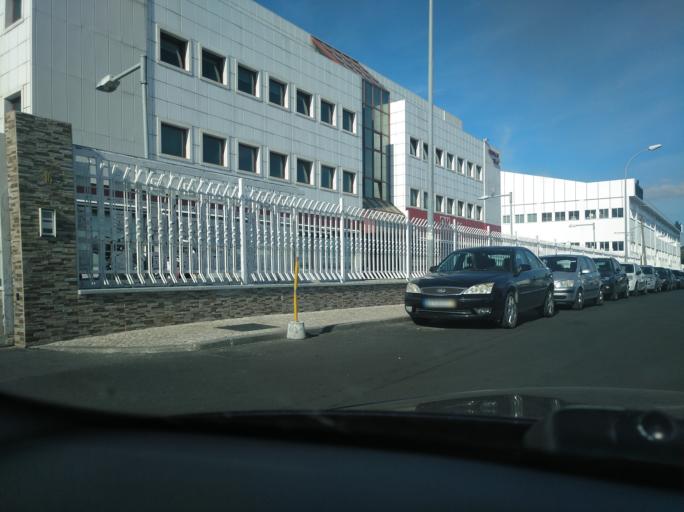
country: PT
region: Lisbon
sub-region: Oeiras
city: Alges
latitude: 38.7237
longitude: -9.2192
